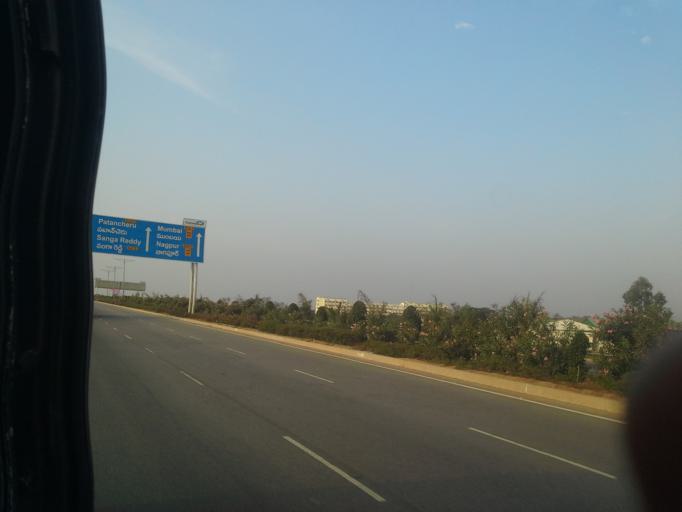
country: IN
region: Telangana
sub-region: Hyderabad
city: Hyderabad
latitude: 17.3364
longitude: 78.3679
